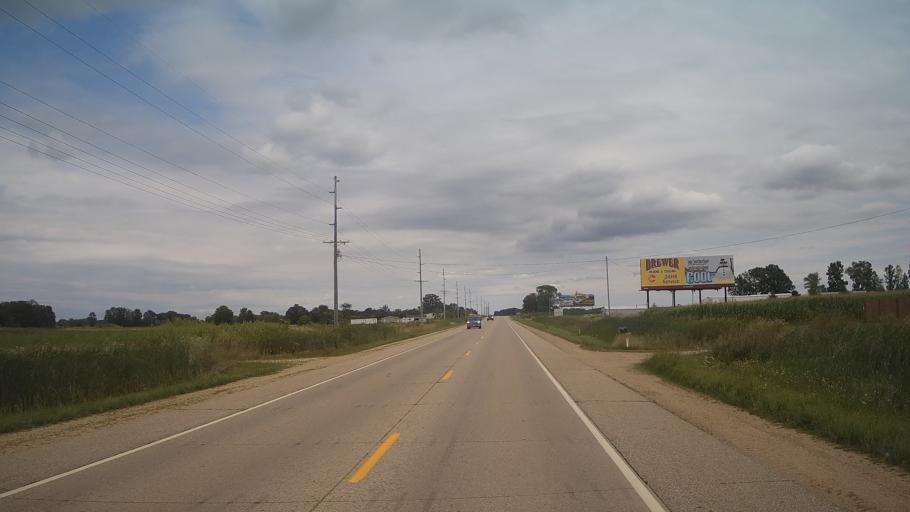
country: US
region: Wisconsin
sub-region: Waushara County
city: Redgranite
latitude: 44.0413
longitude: -89.0230
